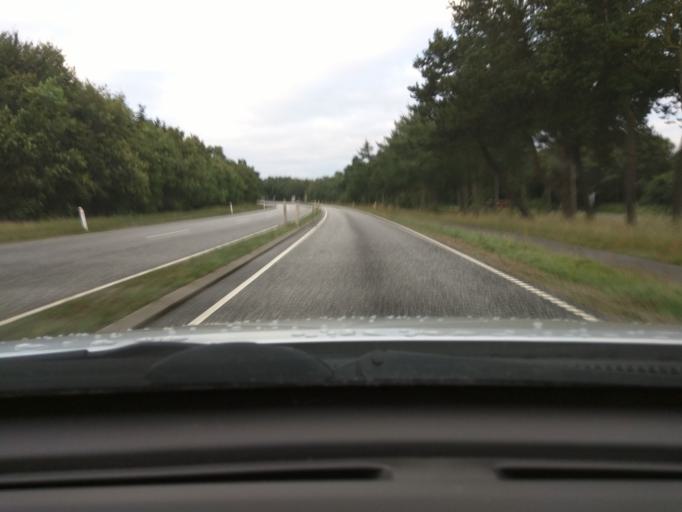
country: DK
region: Central Jutland
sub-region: Viborg Kommune
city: Viborg
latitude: 56.4074
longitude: 9.3716
